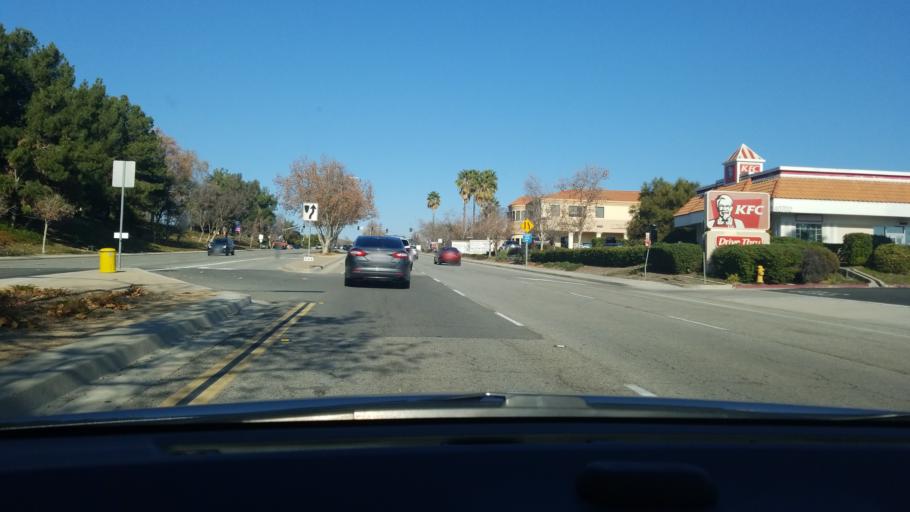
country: US
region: California
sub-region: Riverside County
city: Murrieta
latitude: 33.5701
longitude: -117.2049
